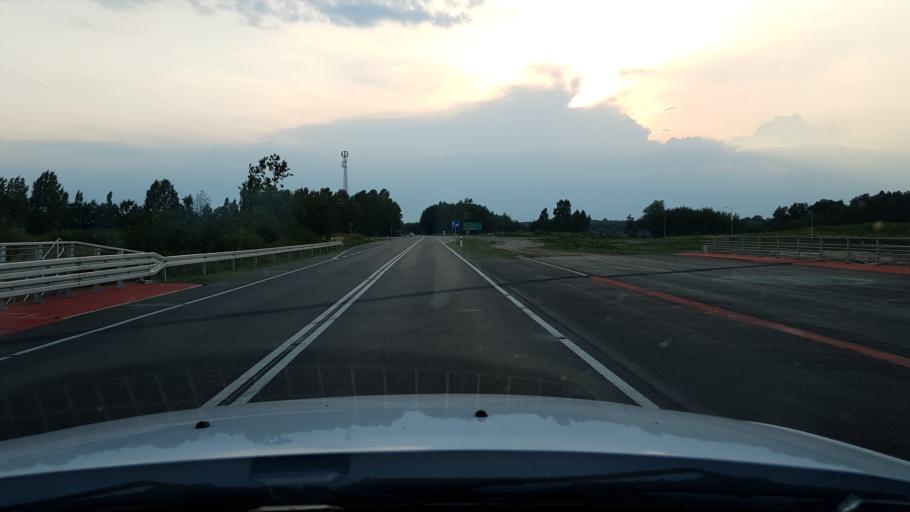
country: PL
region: West Pomeranian Voivodeship
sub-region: Powiat goleniowski
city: Maszewo
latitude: 53.4340
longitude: 15.0772
